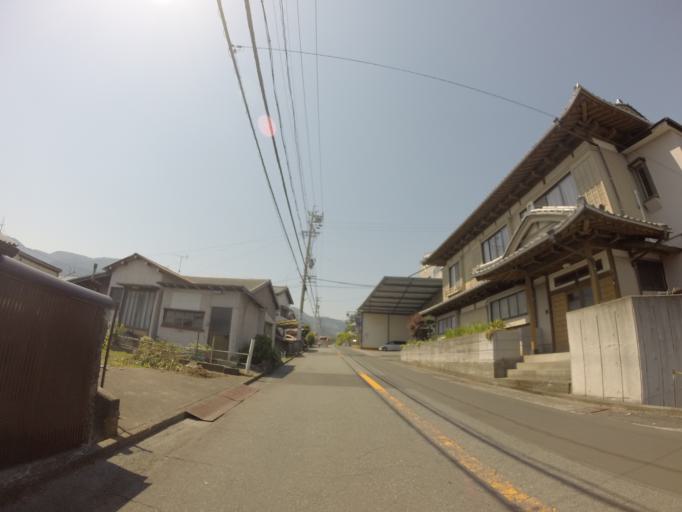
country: JP
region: Shizuoka
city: Fujinomiya
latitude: 35.1093
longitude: 138.5650
